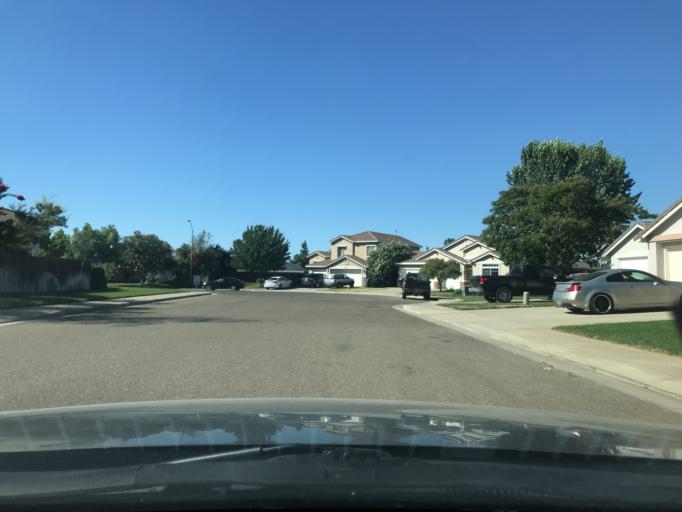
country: US
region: California
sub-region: Merced County
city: Atwater
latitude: 37.3403
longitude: -120.5776
